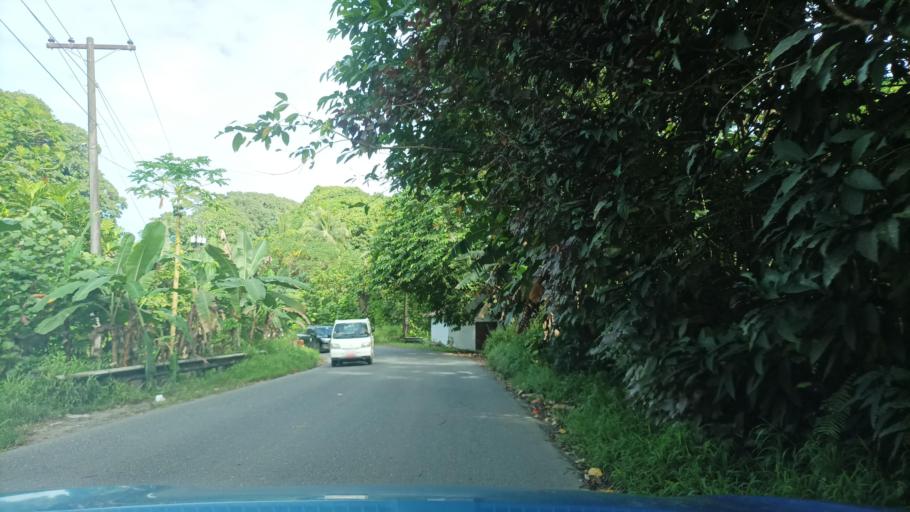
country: FM
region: Pohnpei
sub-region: Kolonia Municipality
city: Kolonia
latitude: 6.9545
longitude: 158.2178
